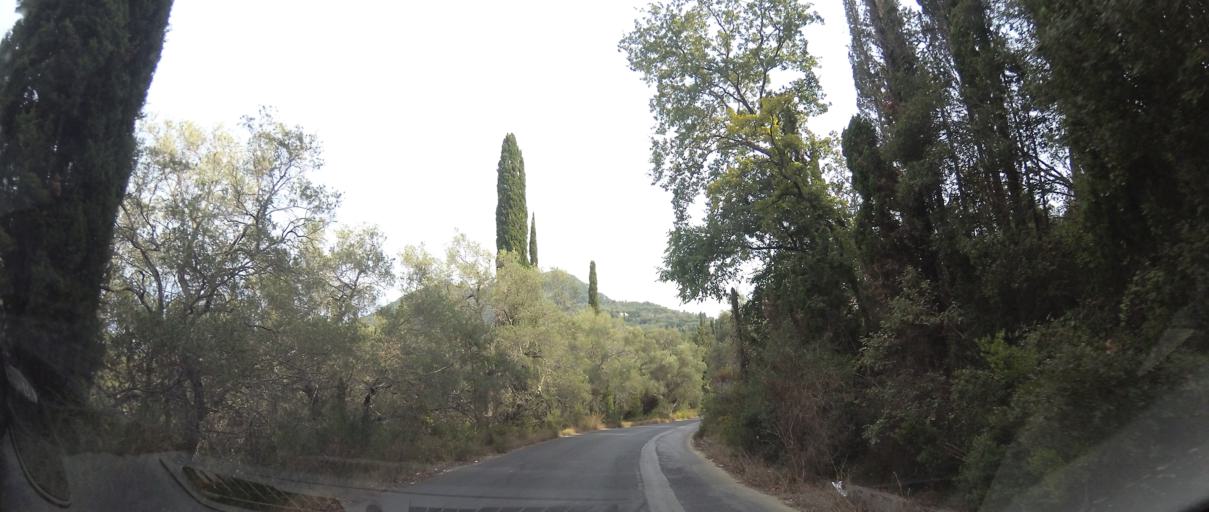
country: GR
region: Ionian Islands
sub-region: Nomos Kerkyras
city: Kynopiastes
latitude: 39.5572
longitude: 19.8589
